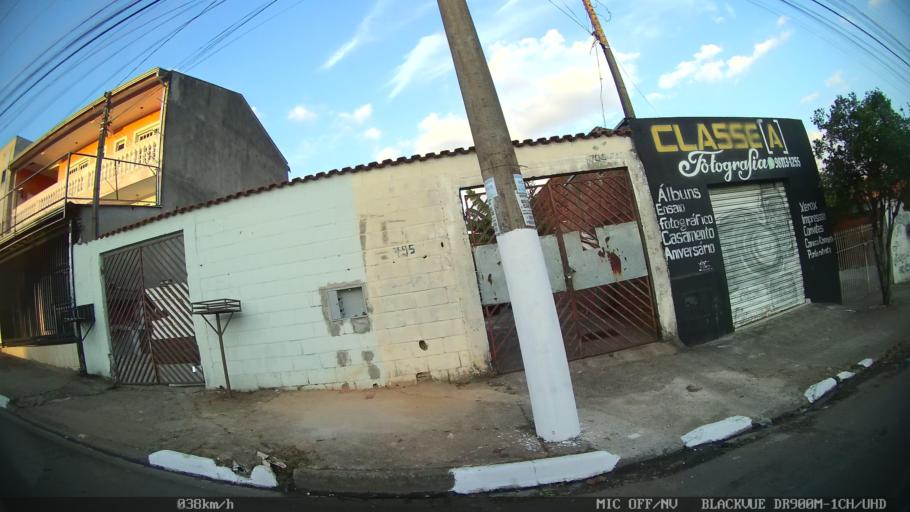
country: BR
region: Sao Paulo
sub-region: Hortolandia
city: Hortolandia
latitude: -22.8563
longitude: -47.2060
